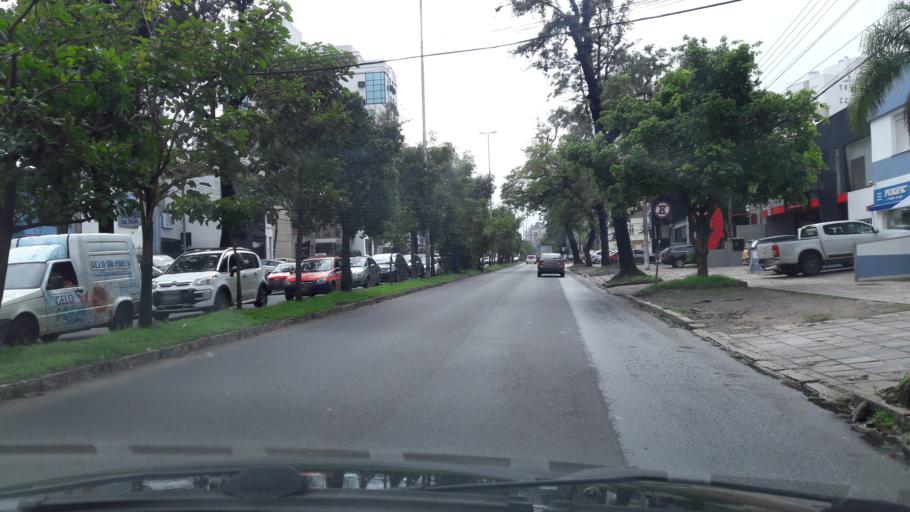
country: BR
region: Rio Grande do Sul
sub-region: Porto Alegre
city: Porto Alegre
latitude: -30.0310
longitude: -51.2025
